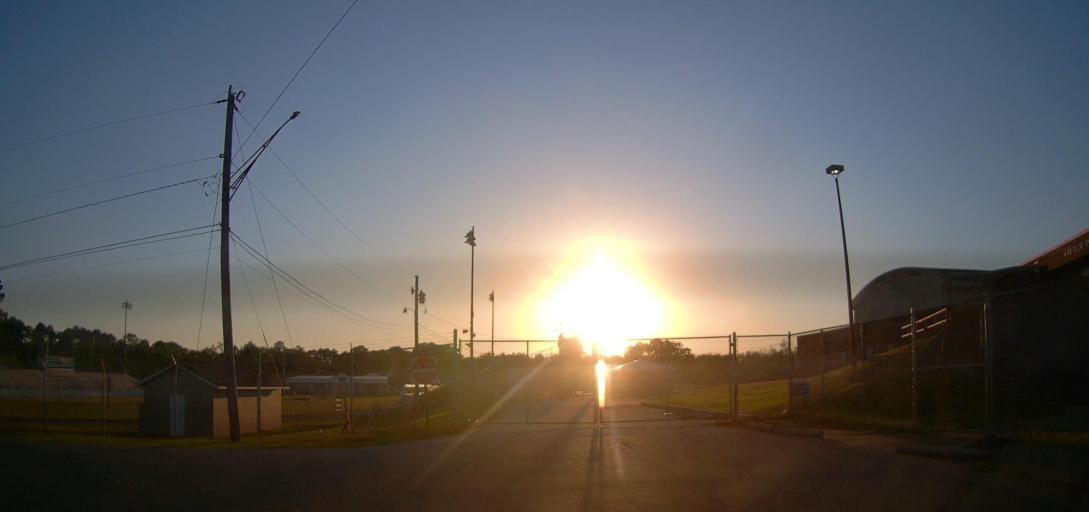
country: US
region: Georgia
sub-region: Ben Hill County
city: Fitzgerald
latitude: 31.7080
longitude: -83.2610
